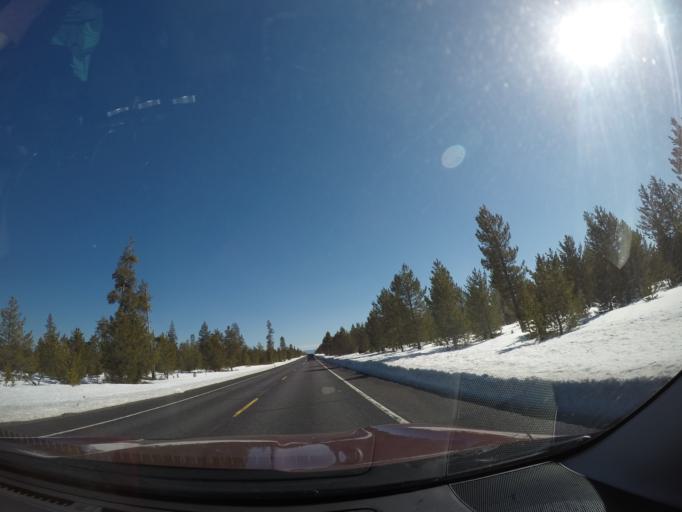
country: US
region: Oregon
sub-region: Deschutes County
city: Three Rivers
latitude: 43.8815
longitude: -121.5692
